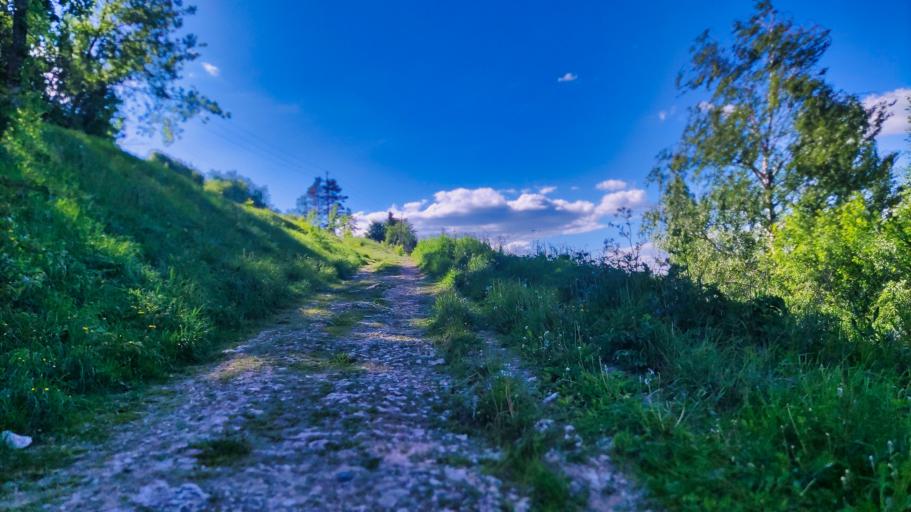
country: RU
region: Tverskaya
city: Rzhev
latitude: 56.2521
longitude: 34.3439
